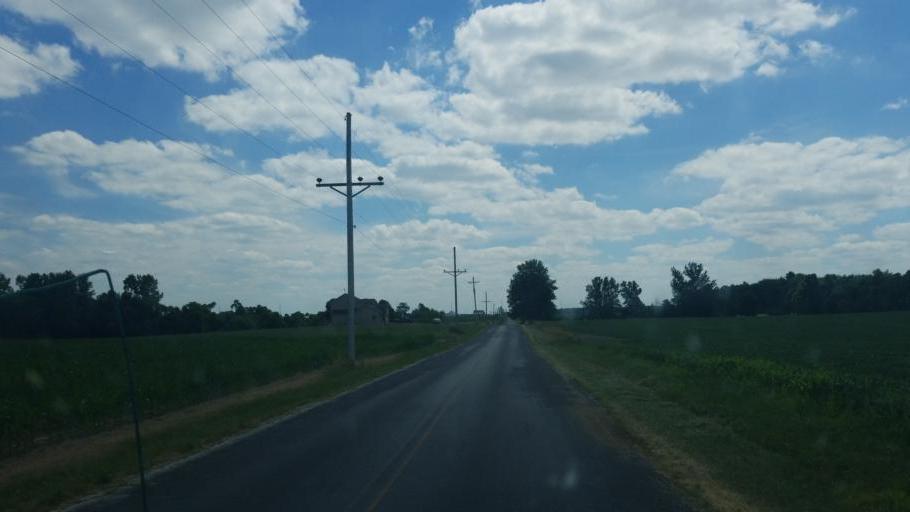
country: US
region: Ohio
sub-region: Williams County
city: Edgerton
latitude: 41.4651
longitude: -84.6912
